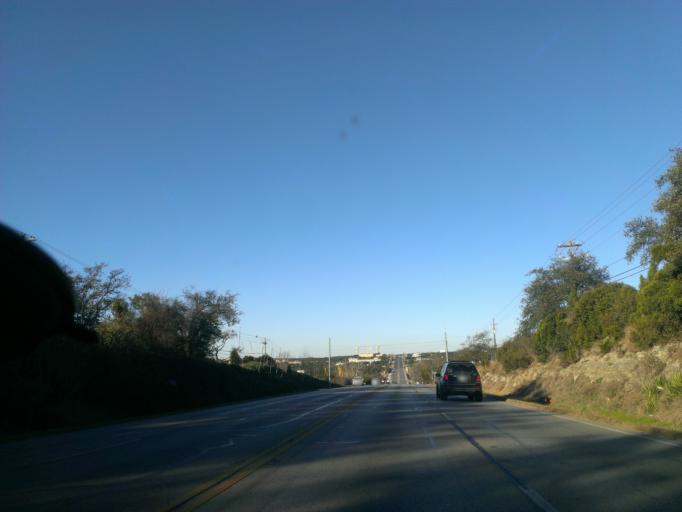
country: US
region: Texas
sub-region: Travis County
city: Barton Creek
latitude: 30.2341
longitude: -97.9145
